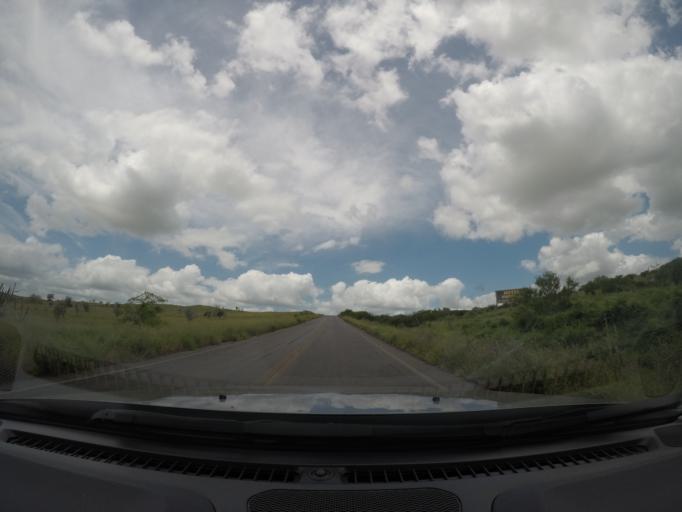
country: BR
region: Bahia
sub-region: Ipira
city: Ipira
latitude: -12.2540
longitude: -39.8170
